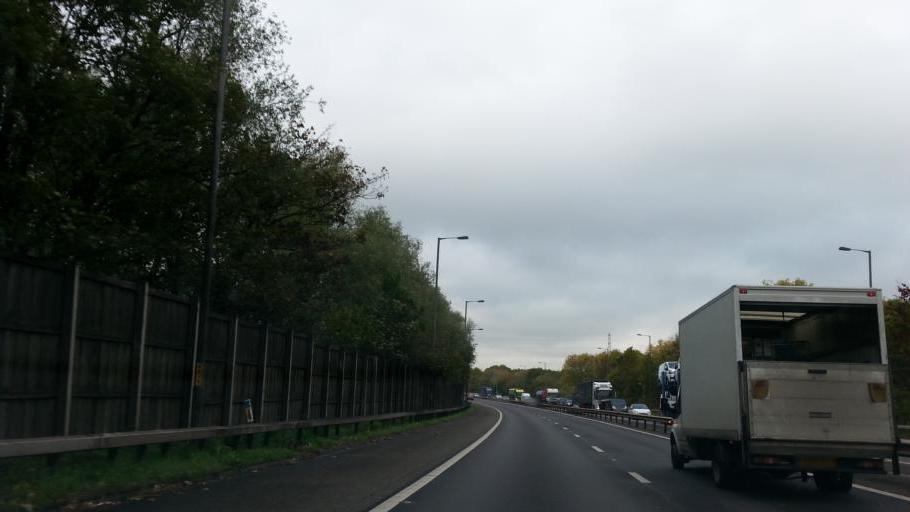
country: GB
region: England
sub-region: Sandwell
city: West Bromwich
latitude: 52.5458
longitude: -1.9673
